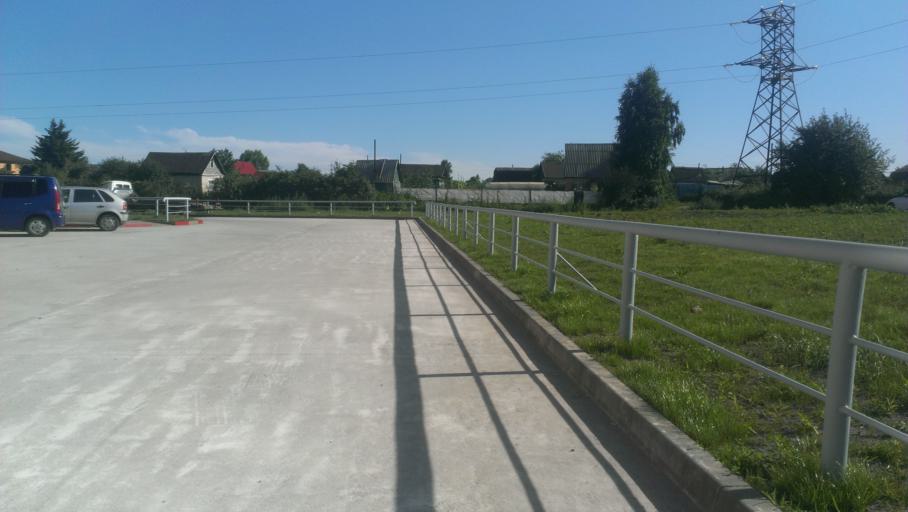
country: RU
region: Altai Krai
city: Novosilikatnyy
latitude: 53.3263
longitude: 83.6673
